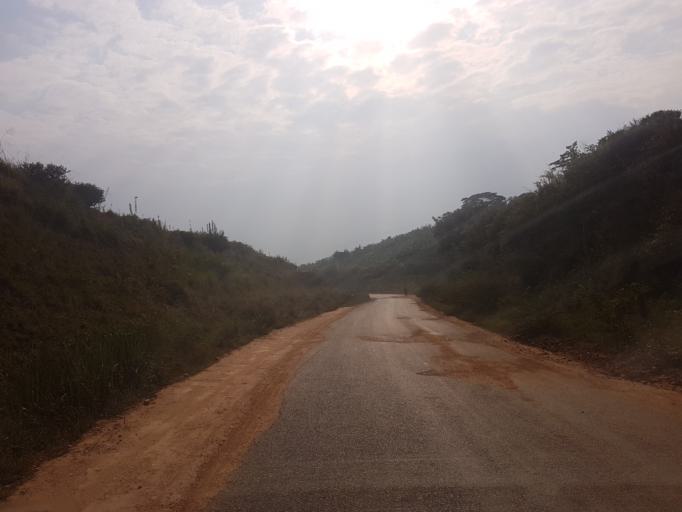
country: UG
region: Western Region
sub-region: Bushenyi District
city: Bushenyi
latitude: -0.4412
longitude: 30.1117
